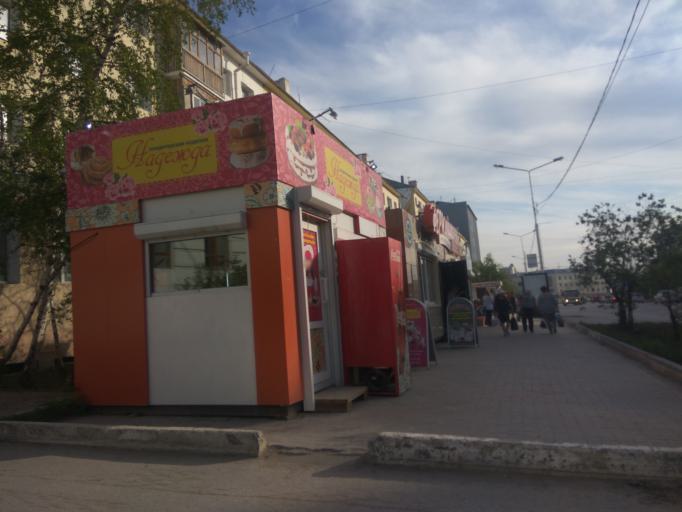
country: RU
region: Sakha
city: Yakutsk
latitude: 62.0245
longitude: 129.7244
